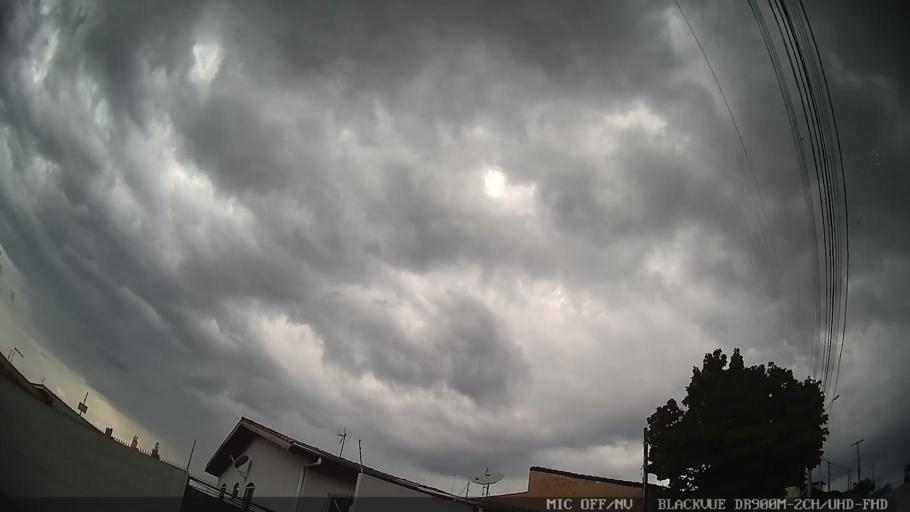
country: BR
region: Sao Paulo
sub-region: Itatiba
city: Itatiba
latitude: -23.0106
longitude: -46.8583
